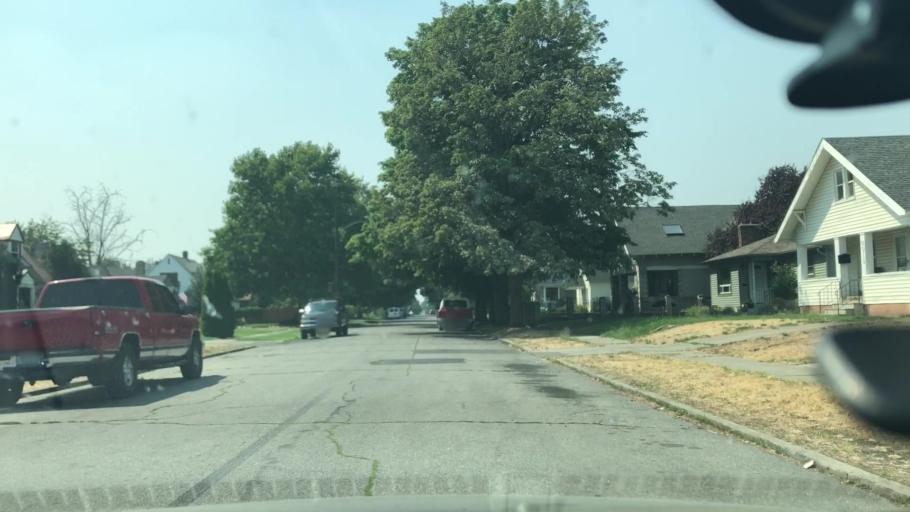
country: US
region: Washington
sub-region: Spokane County
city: Spokane
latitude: 47.6876
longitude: -117.3794
